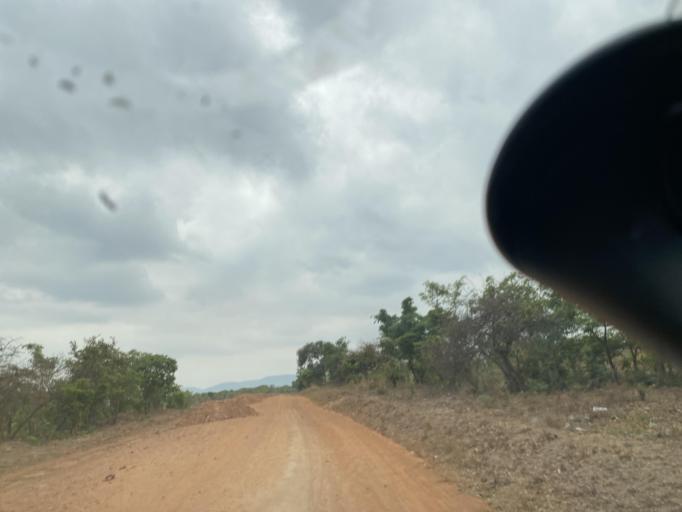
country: ZM
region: Lusaka
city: Chongwe
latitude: -15.2509
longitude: 28.7274
